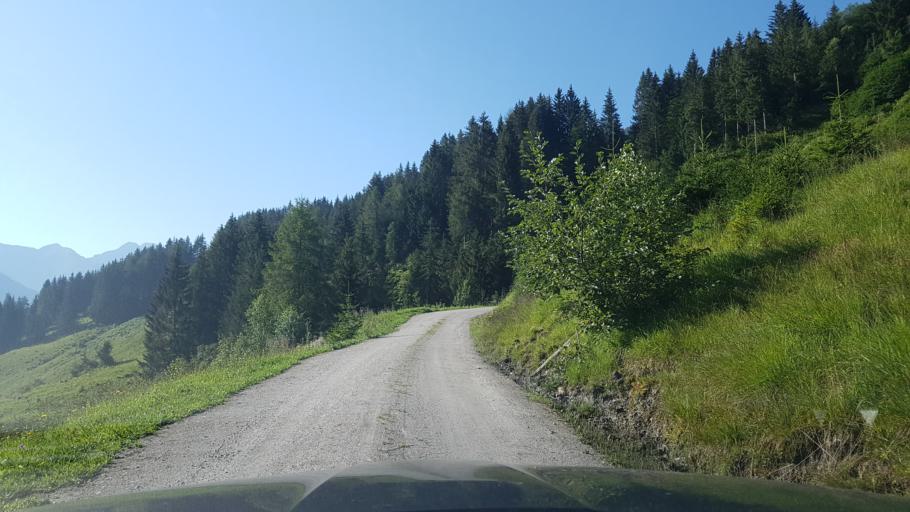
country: AT
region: Salzburg
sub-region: Politischer Bezirk Sankt Johann im Pongau
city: Dorfgastein
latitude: 47.2555
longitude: 13.0786
